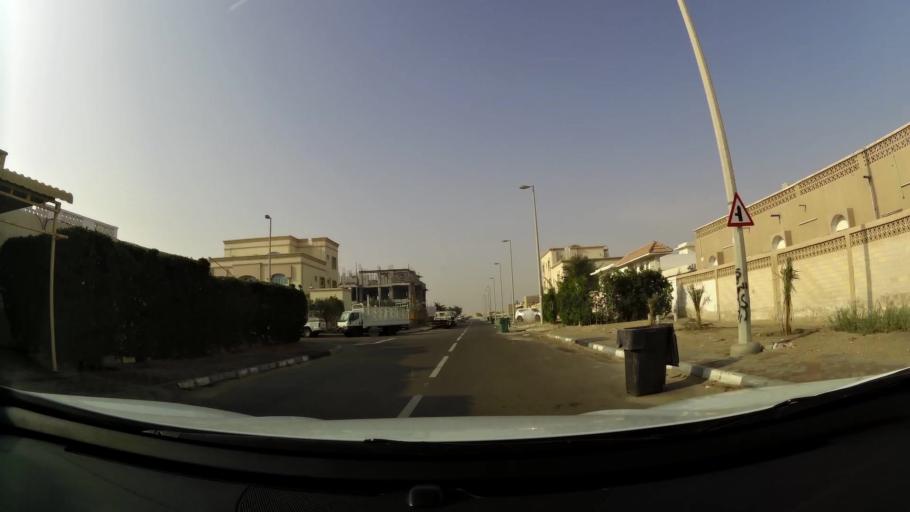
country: AE
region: Abu Dhabi
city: Abu Dhabi
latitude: 24.2726
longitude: 54.6421
